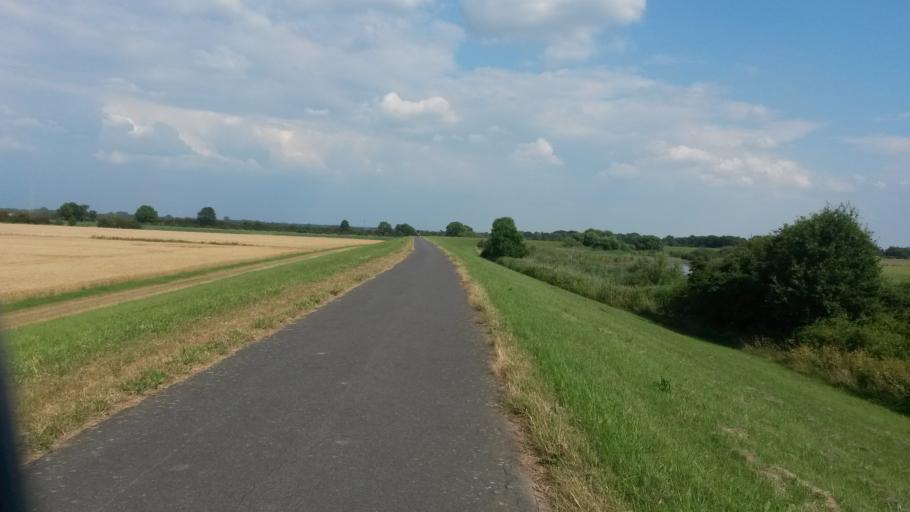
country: DE
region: Lower Saxony
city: Riede
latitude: 53.0173
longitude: 8.9167
